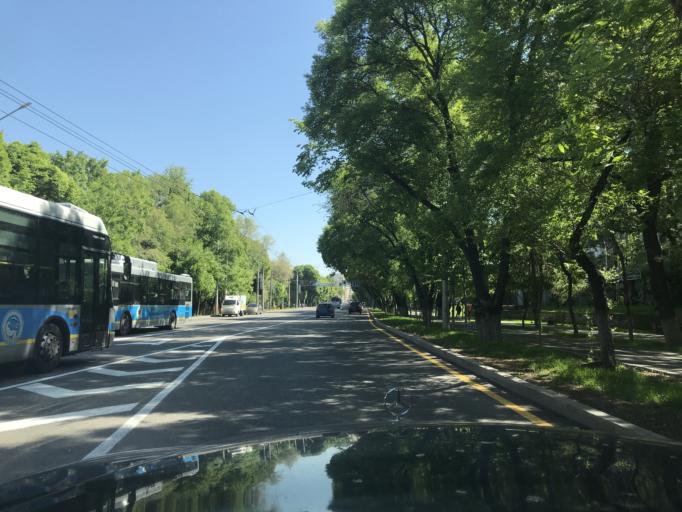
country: KZ
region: Almaty Qalasy
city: Almaty
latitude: 43.2281
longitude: 76.9300
